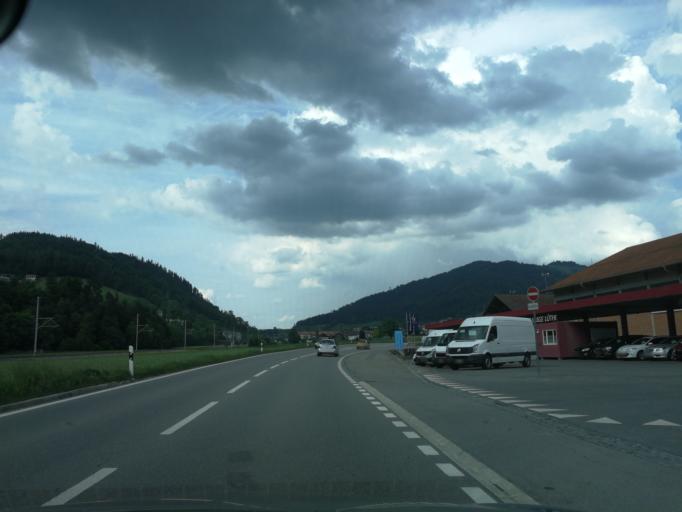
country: CH
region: Lucerne
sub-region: Entlebuch District
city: Oberdiessbach
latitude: 46.8307
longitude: 7.6136
